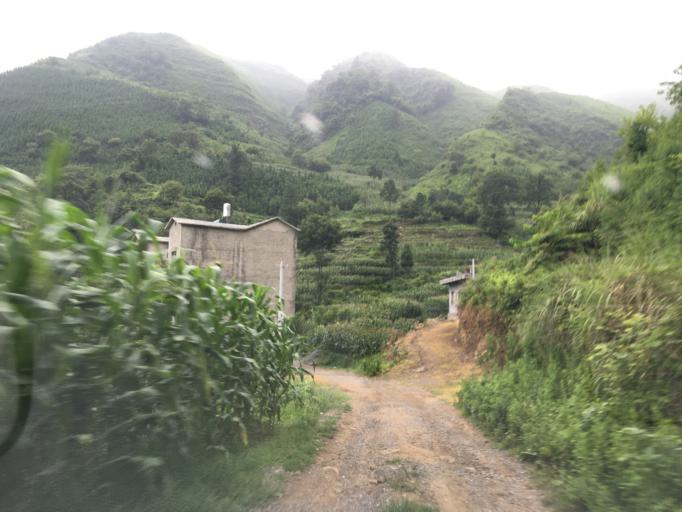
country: CN
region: Guangxi Zhuangzu Zizhiqu
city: Xinzhou
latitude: 24.9884
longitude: 105.6391
